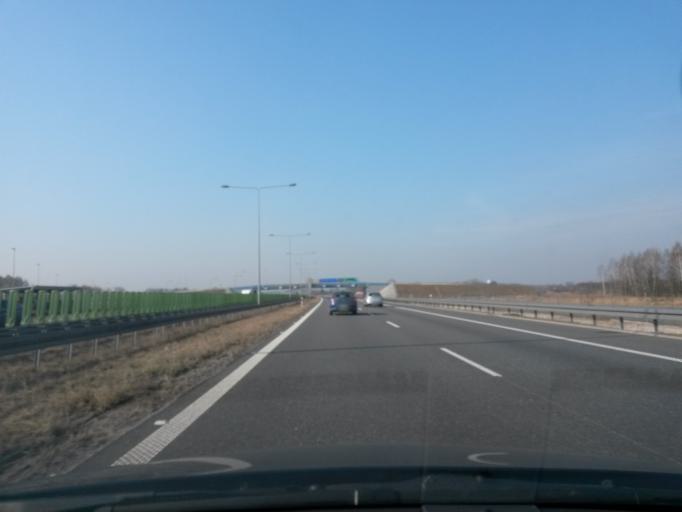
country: PL
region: Lodz Voivodeship
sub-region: powiat Lowicki
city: Nieborow
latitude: 52.0453
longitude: 20.0564
